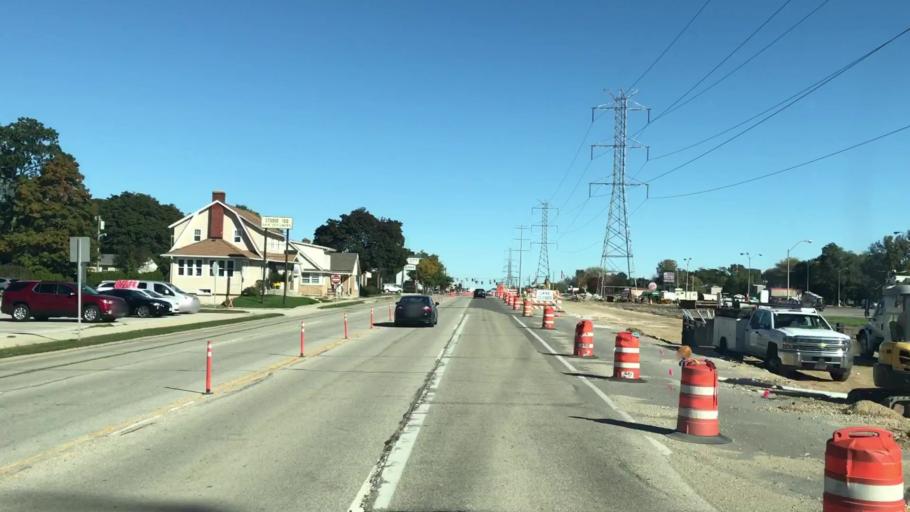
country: US
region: Wisconsin
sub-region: Milwaukee County
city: Hales Corners
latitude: 42.9411
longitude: -88.0485
